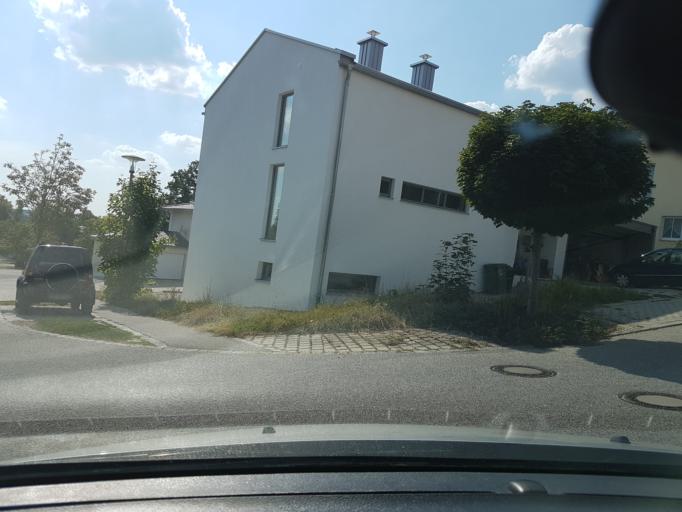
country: DE
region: Bavaria
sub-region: Lower Bavaria
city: Vilsbiburg
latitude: 48.4311
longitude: 12.3548
